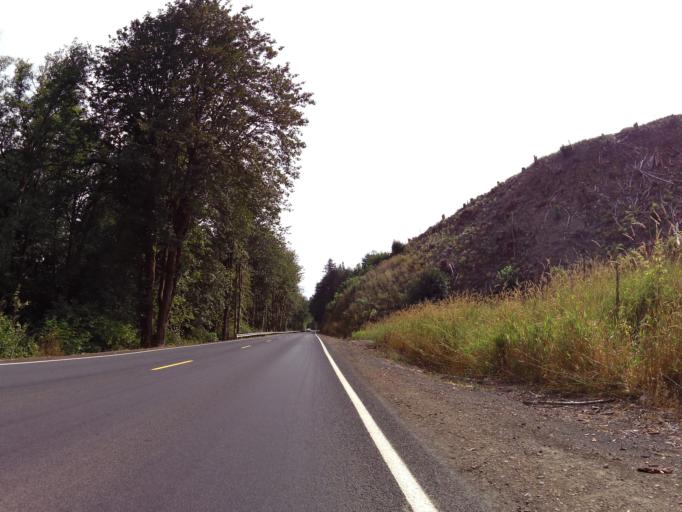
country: US
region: Washington
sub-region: Cowlitz County
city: Castle Rock
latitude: 46.3427
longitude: -122.9387
